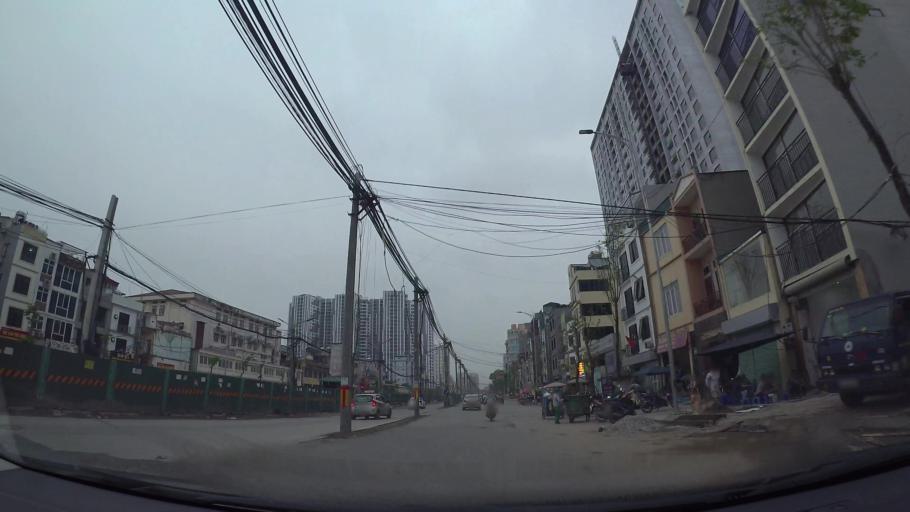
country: VN
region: Ha Noi
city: Hai BaTrung
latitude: 20.9966
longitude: 105.8631
